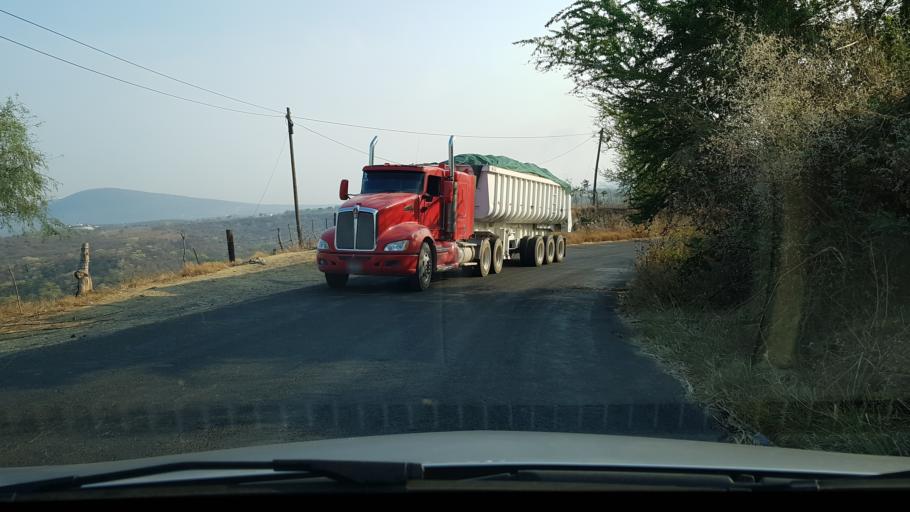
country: MX
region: Morelos
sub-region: Tepalcingo
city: Zacapalco
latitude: 18.6313
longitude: -99.0101
